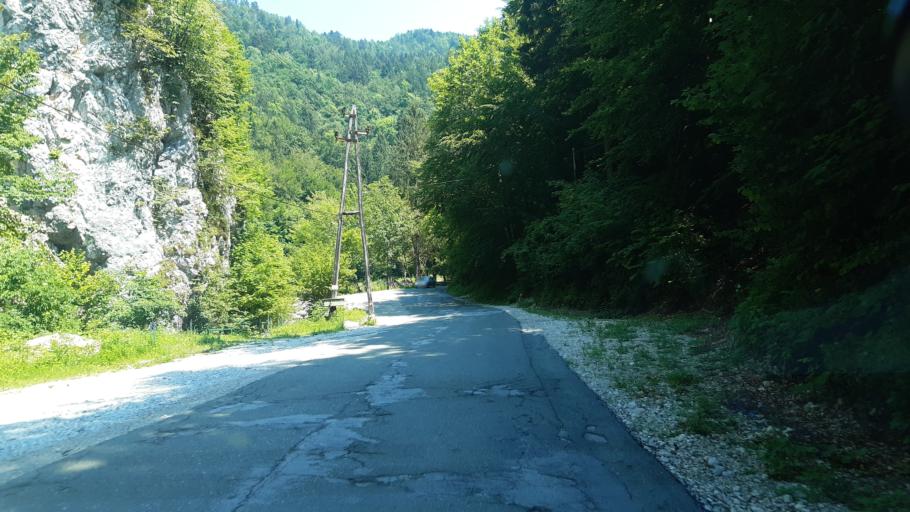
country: SI
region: Cerklje na Gorenjskem
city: Cerklje na Gorenjskem
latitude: 46.2832
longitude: 14.4947
